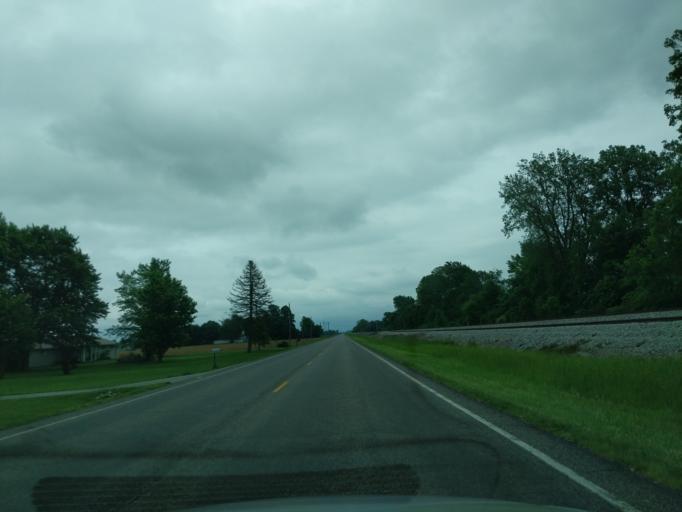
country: US
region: Indiana
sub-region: Madison County
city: Elwood
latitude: 40.2811
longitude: -85.9250
